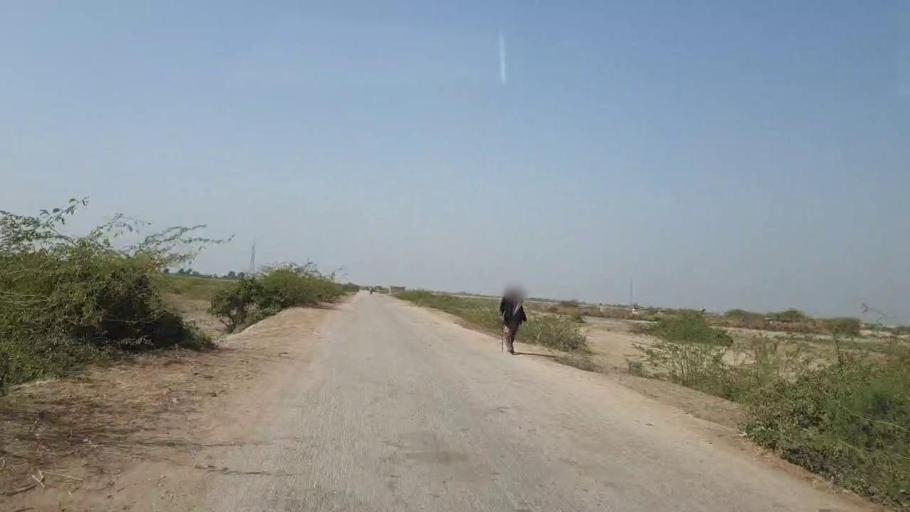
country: PK
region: Sindh
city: Naukot
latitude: 25.0153
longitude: 69.4616
